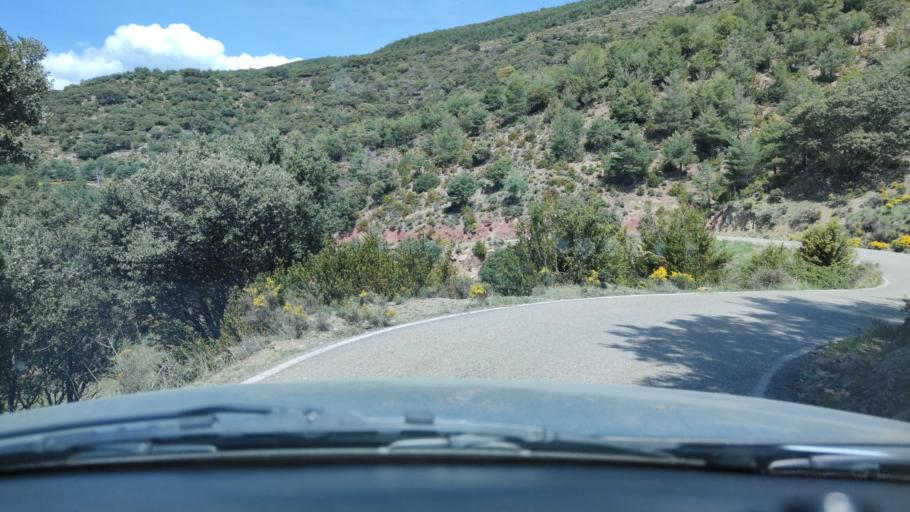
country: ES
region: Catalonia
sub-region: Provincia de Lleida
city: Sort
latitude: 42.3062
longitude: 1.1215
